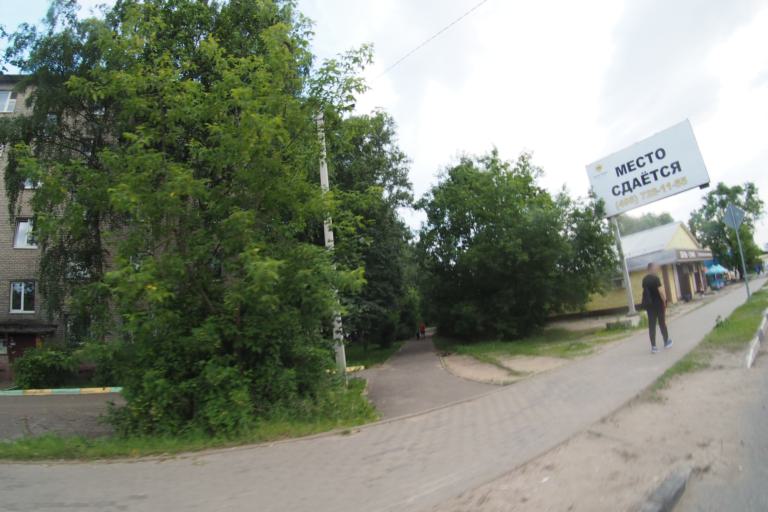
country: RU
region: Moskovskaya
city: Dedovsk
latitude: 55.8652
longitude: 37.1229
